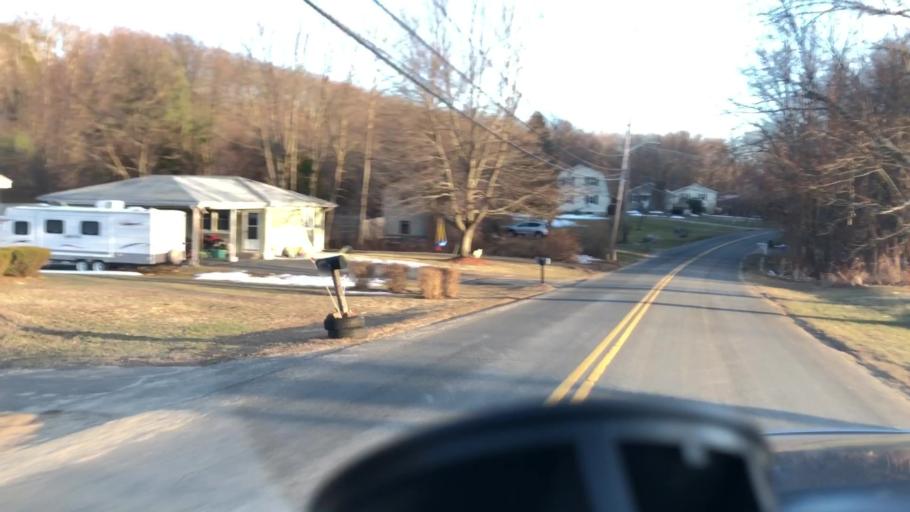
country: US
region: Massachusetts
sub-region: Hampshire County
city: Southampton
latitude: 42.2033
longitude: -72.6796
